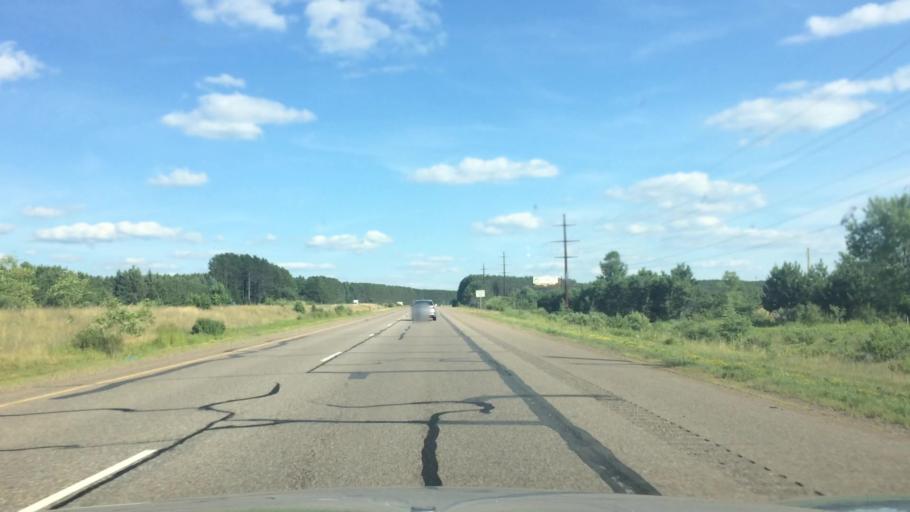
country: US
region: Wisconsin
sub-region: Lincoln County
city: Merrill
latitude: 45.2025
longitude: -89.6568
